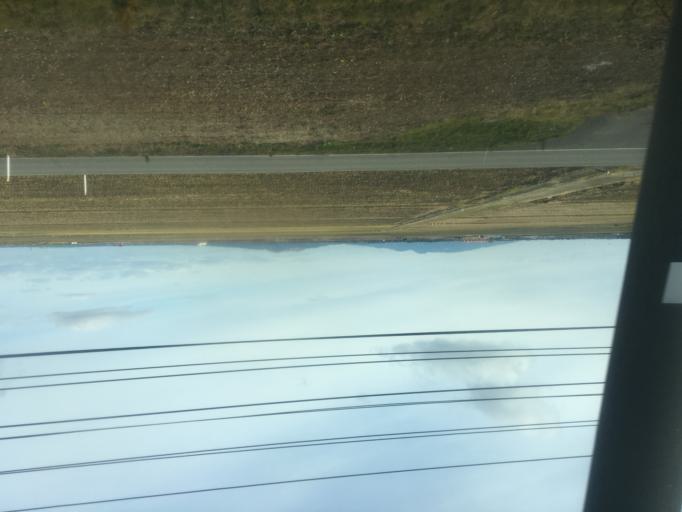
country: JP
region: Akita
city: Tenno
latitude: 39.8740
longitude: 140.0640
